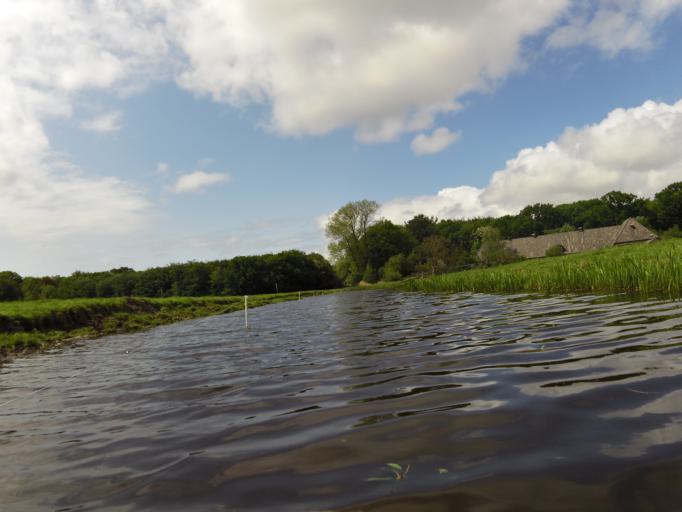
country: NL
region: South Holland
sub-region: Gemeente Wassenaar
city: Wassenaar
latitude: 52.1265
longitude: 4.4042
